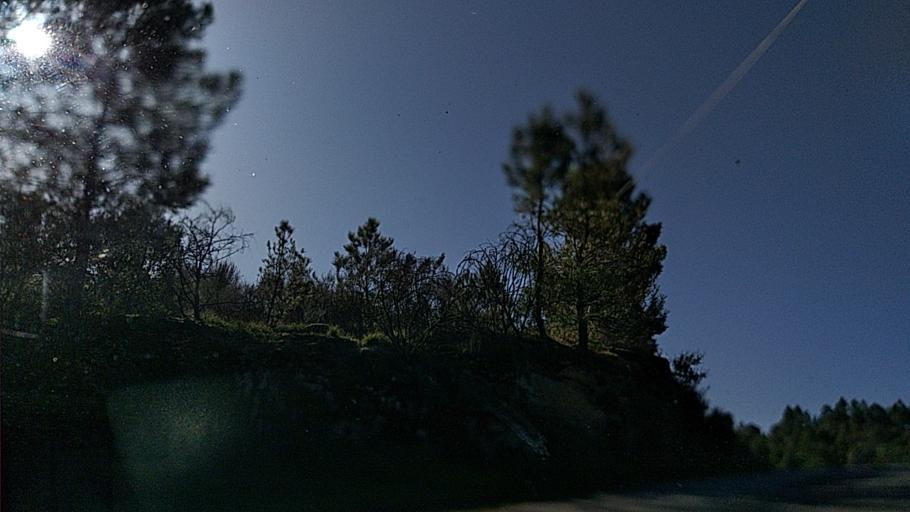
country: PT
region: Guarda
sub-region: Celorico da Beira
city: Celorico da Beira
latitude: 40.6819
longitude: -7.3971
